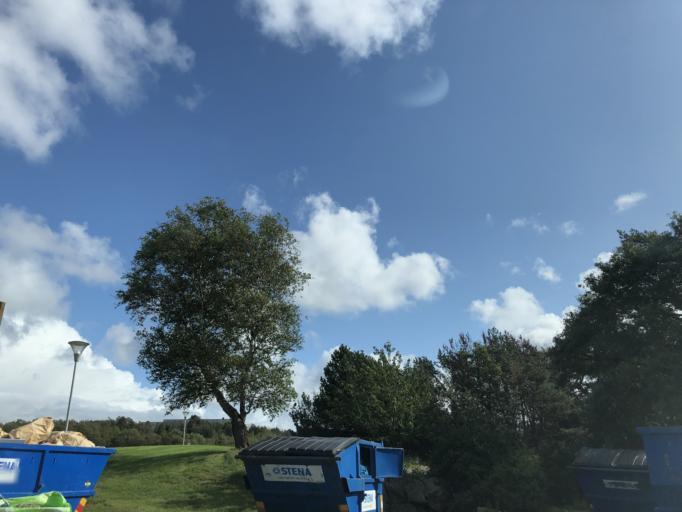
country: SE
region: Vaestra Goetaland
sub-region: Goteborg
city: Majorna
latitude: 57.7251
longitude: 11.8482
